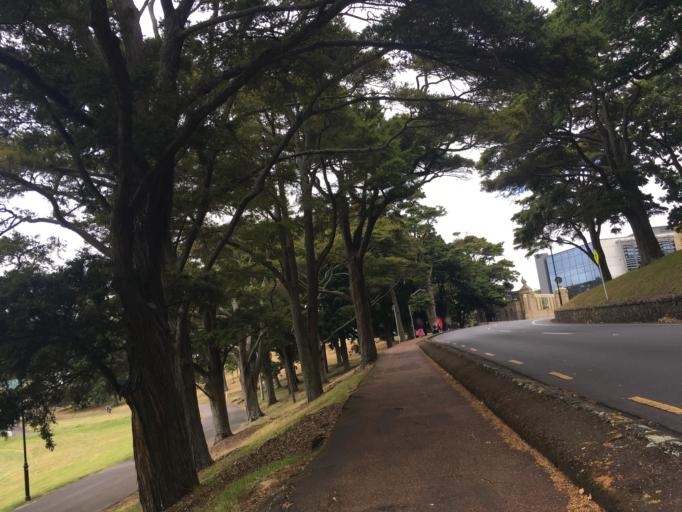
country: NZ
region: Auckland
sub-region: Auckland
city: Auckland
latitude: -36.8614
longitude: 174.7714
